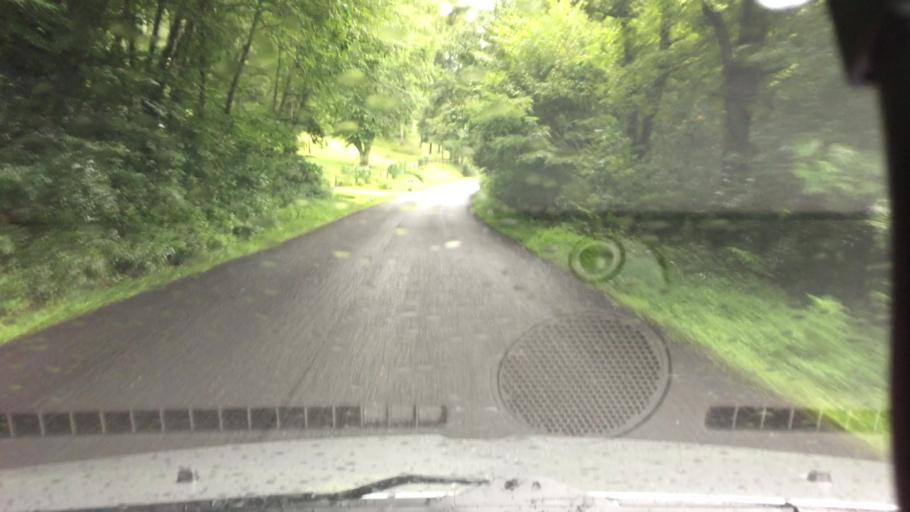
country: US
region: North Carolina
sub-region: Madison County
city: Mars Hill
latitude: 35.9133
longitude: -82.4969
